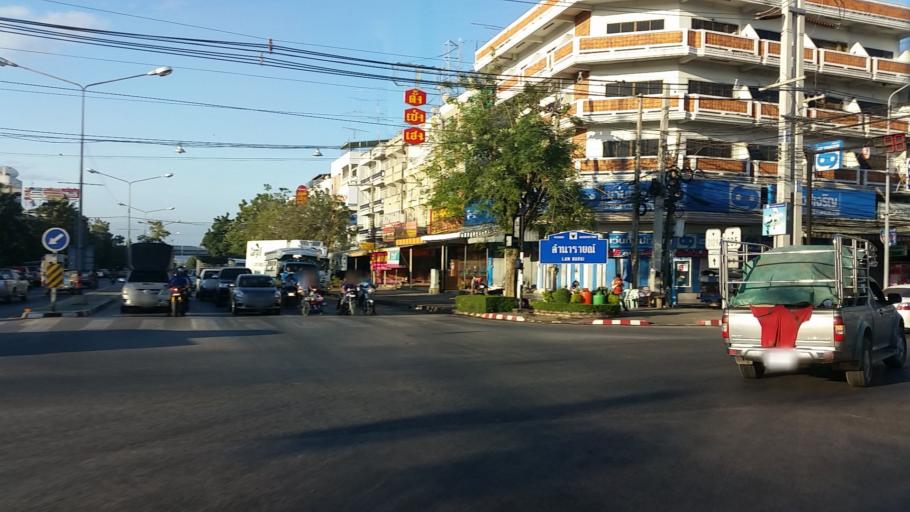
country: TH
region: Lop Buri
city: Chai Badan
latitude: 15.2075
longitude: 101.1340
